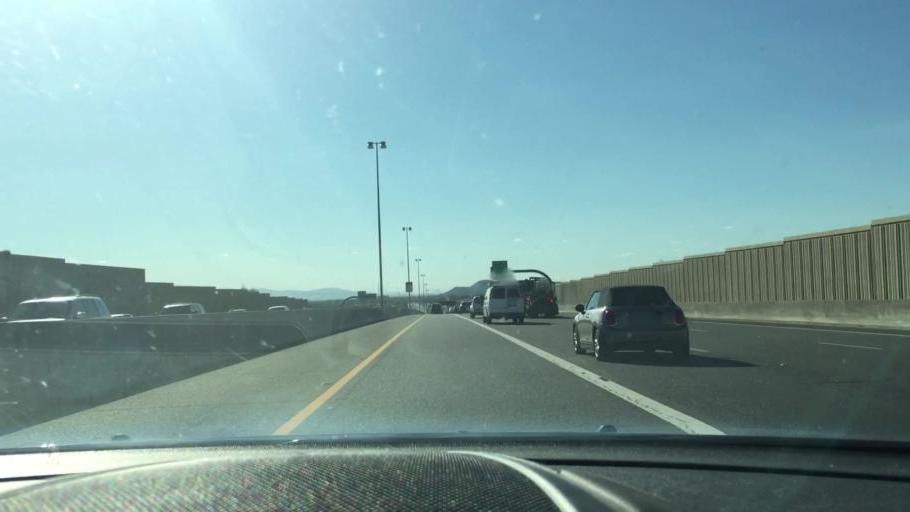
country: US
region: Arizona
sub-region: Maricopa County
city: Paradise Valley
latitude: 33.6705
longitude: -112.0479
